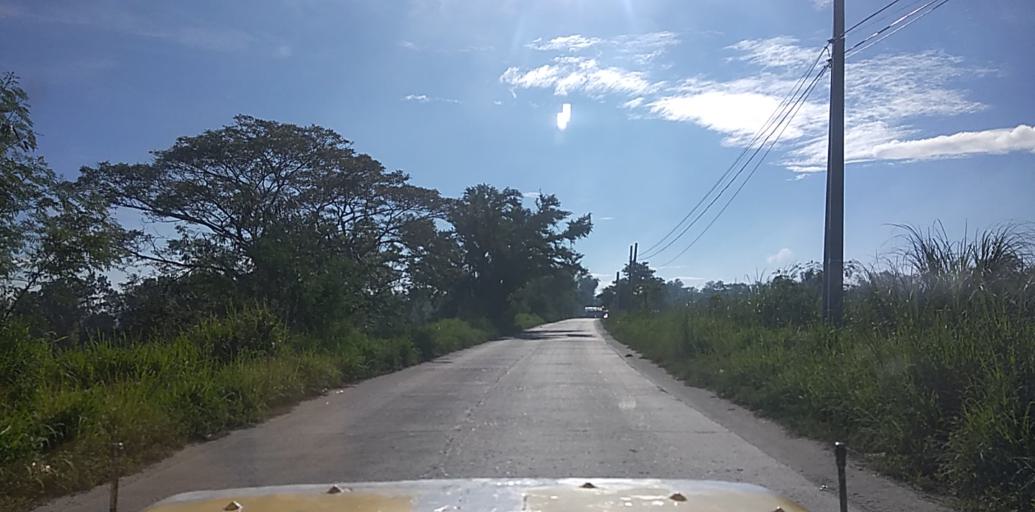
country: PH
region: Central Luzon
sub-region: Province of Pampanga
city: Anao
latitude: 15.1204
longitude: 120.7016
